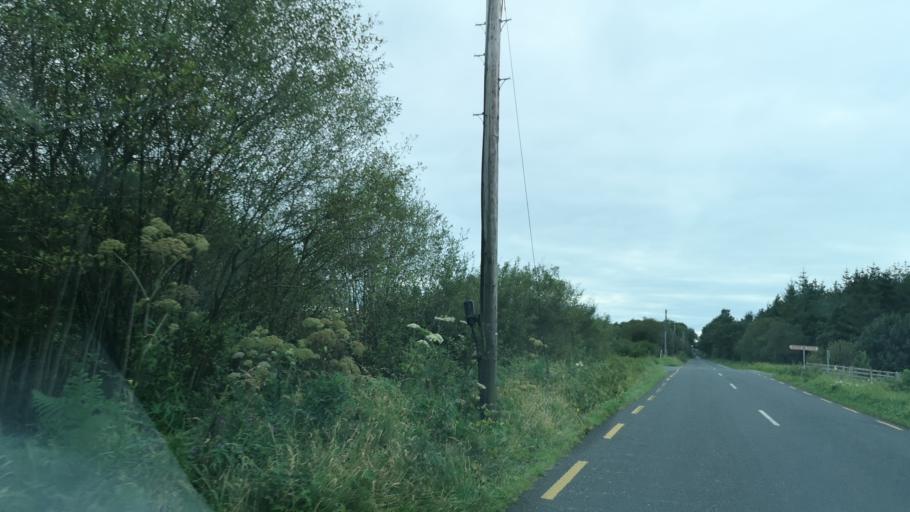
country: IE
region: Leinster
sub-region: Uibh Fhaili
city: Ferbane
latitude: 53.2308
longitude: -7.7724
